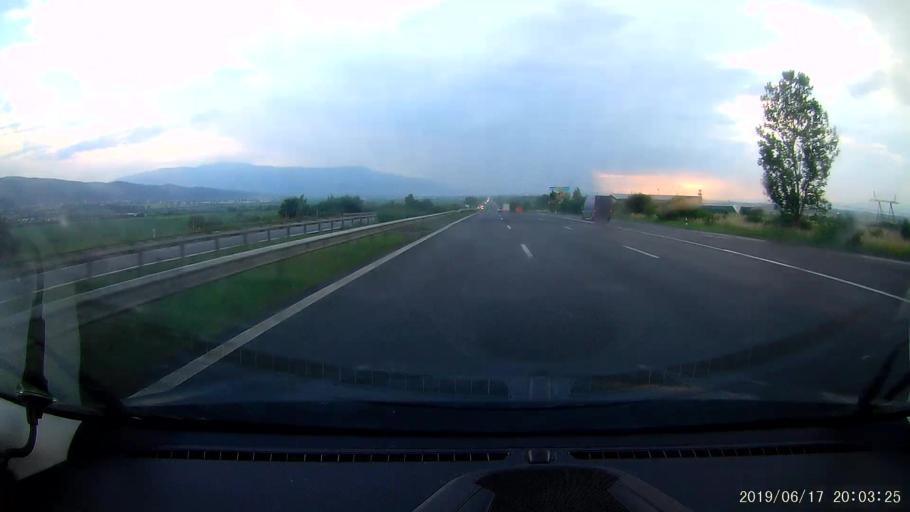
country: BG
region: Sofiya
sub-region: Obshtina Elin Pelin
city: Elin Pelin
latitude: 42.6249
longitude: 23.5114
